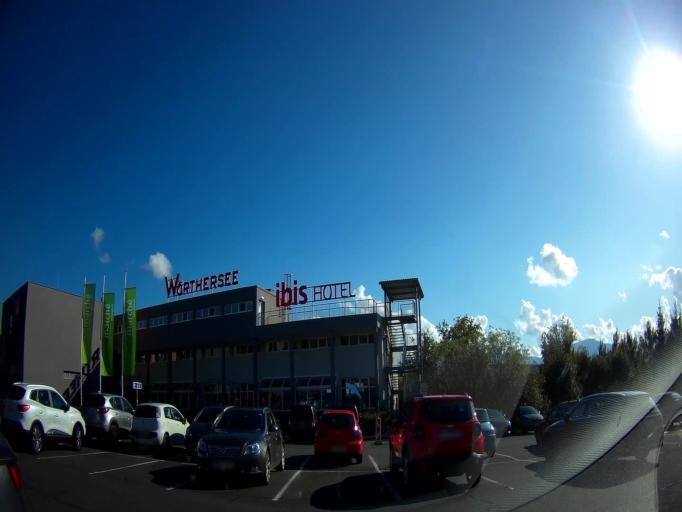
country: AT
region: Carinthia
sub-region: Politischer Bezirk Klagenfurt Land
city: Schiefling am See
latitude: 46.6298
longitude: 14.0945
